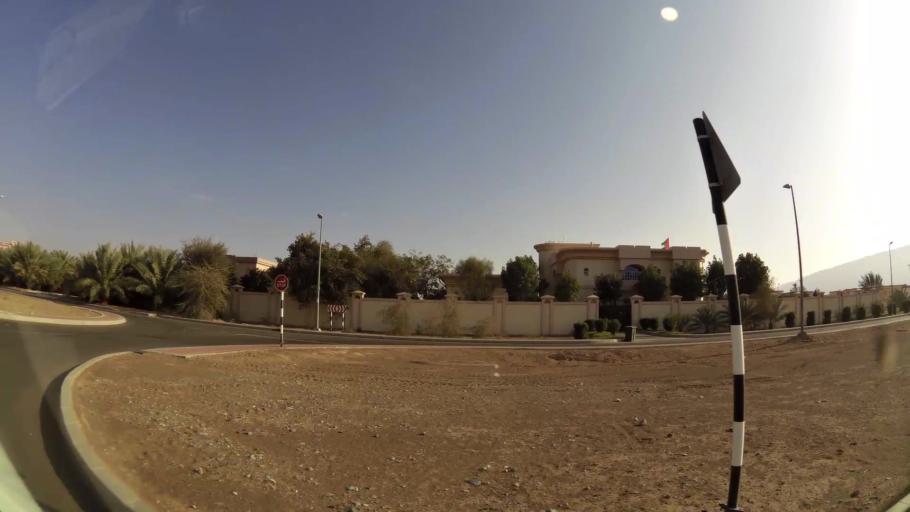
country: AE
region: Abu Dhabi
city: Al Ain
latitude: 24.0717
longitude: 55.8467
